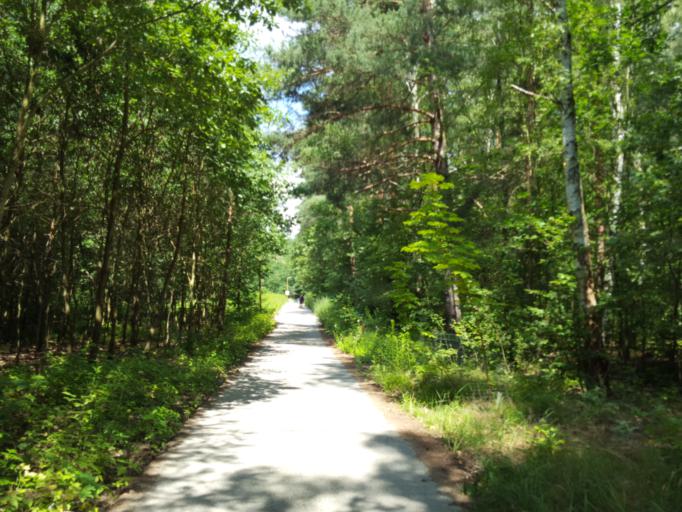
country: DE
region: Saxony
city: Albertstadt
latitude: 51.1188
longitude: 13.7970
